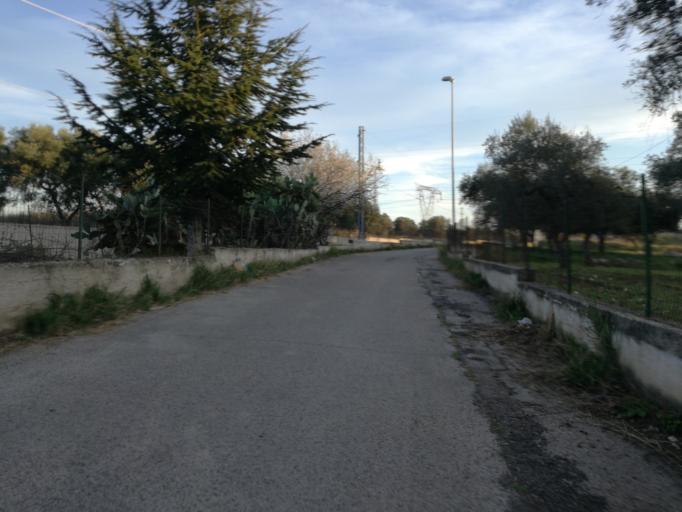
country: IT
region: Apulia
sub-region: Provincia di Bari
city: Lamie
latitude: 41.0315
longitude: 16.8780
